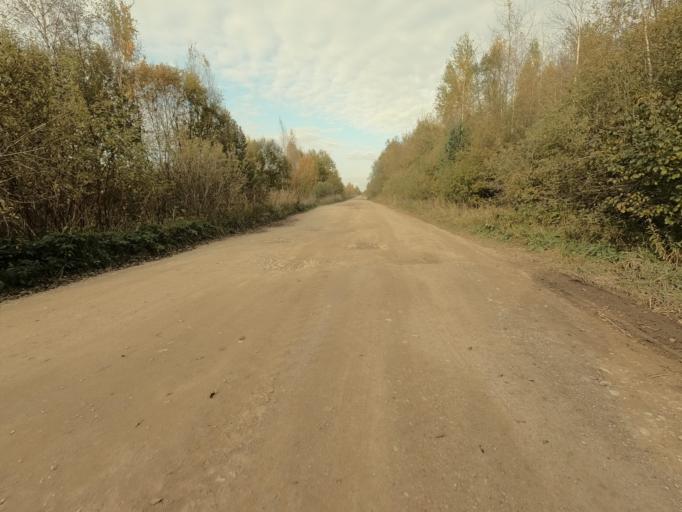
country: RU
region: Novgorod
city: Volkhovskiy
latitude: 58.9095
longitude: 31.0389
